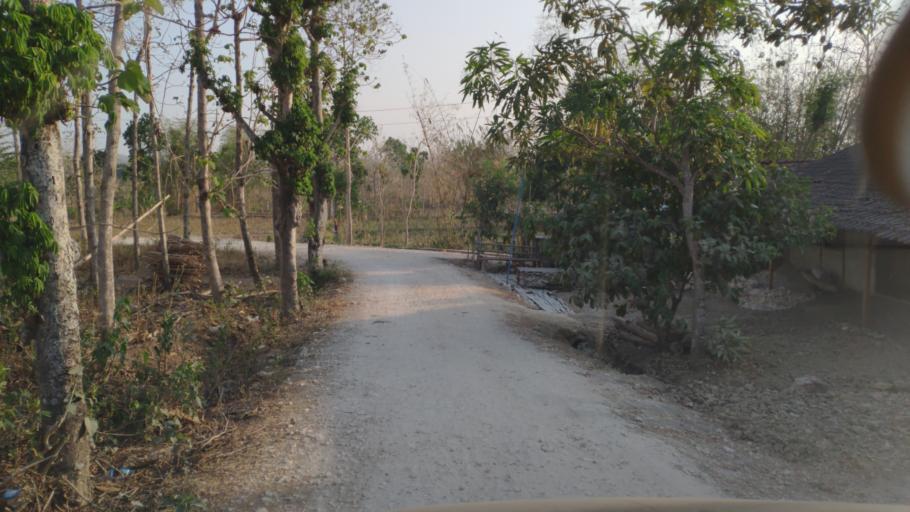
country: ID
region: Central Java
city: Jepang Satu
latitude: -7.0269
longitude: 111.4272
